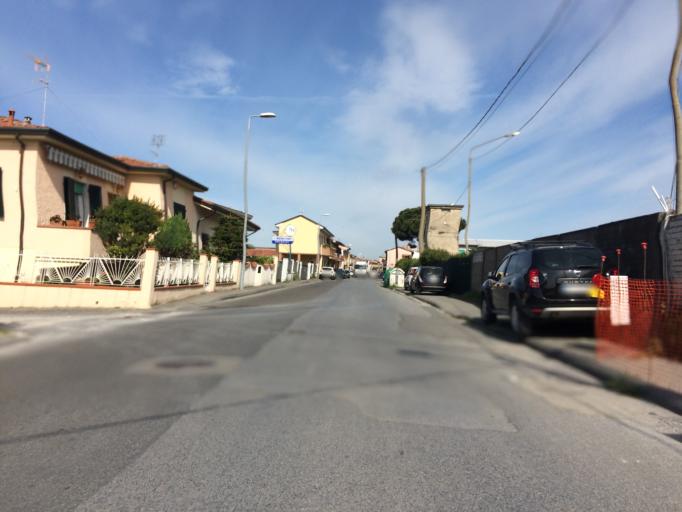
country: IT
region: Tuscany
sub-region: Provincia di Massa-Carrara
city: Carrara
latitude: 44.0432
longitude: 10.0715
